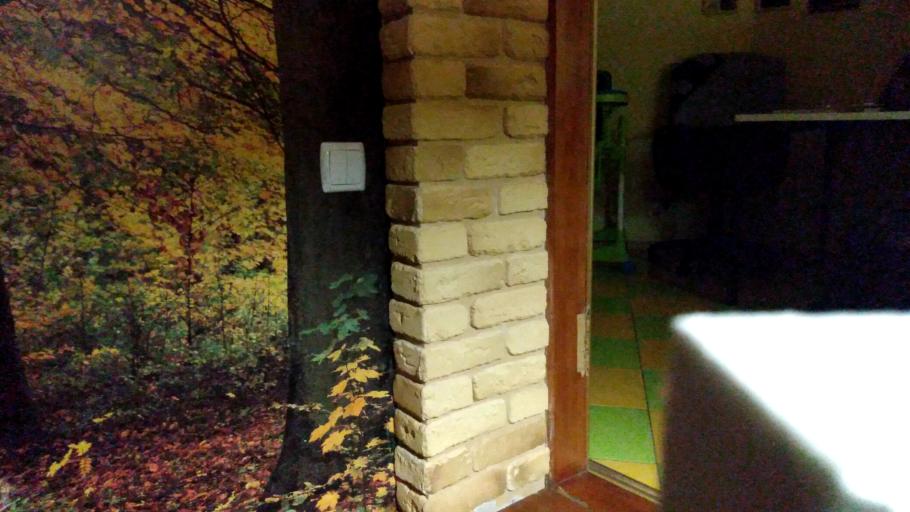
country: RU
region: Vologda
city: Lipin Bor
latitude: 61.1597
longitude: 37.9031
